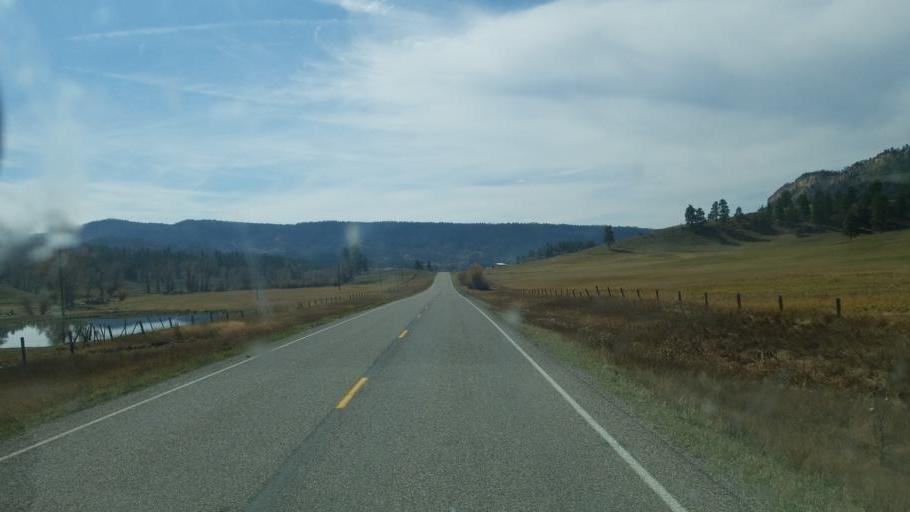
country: US
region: New Mexico
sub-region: Rio Arriba County
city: Dulce
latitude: 37.0563
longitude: -106.8387
